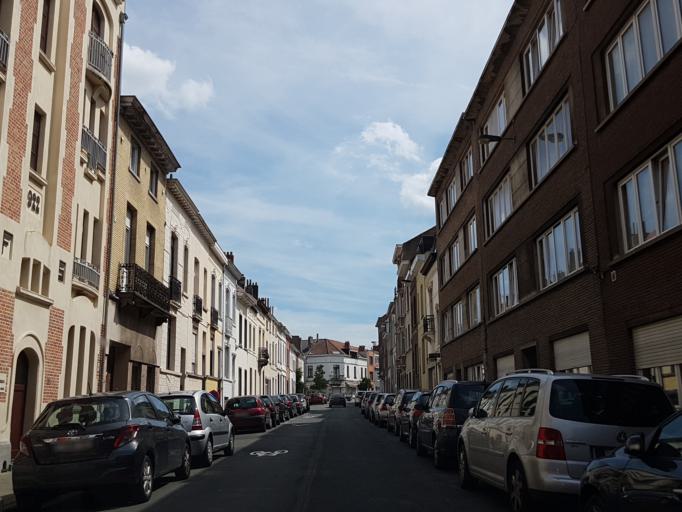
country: BE
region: Brussels Capital
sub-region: Bruxelles-Capitale
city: Brussels
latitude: 50.8698
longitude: 4.3919
